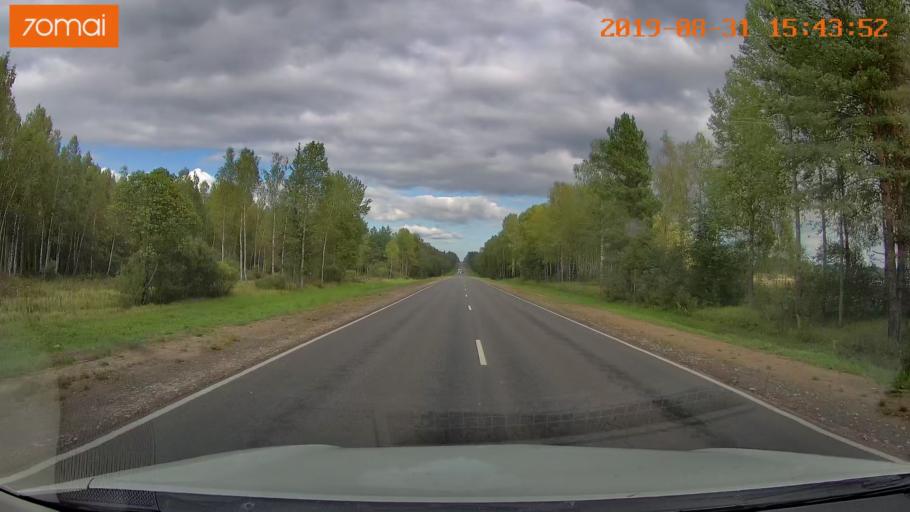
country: RU
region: Kaluga
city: Mosal'sk
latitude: 54.6552
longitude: 34.9187
